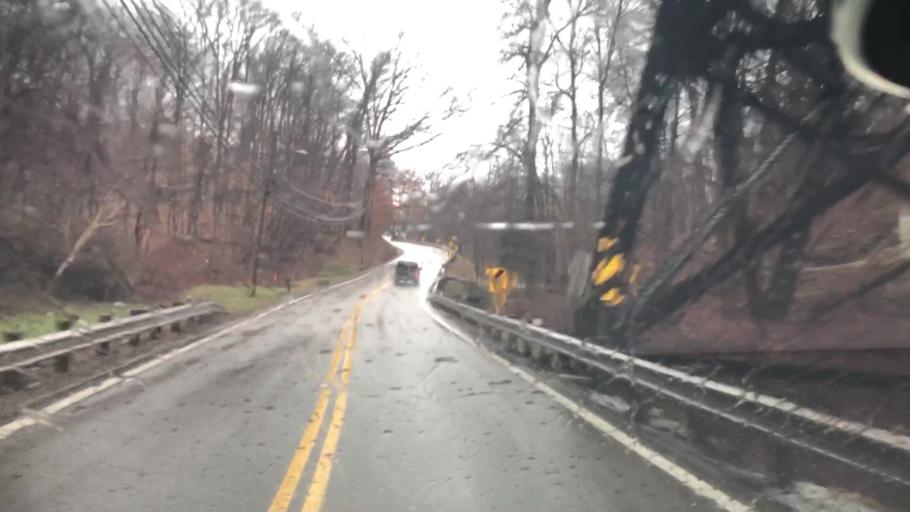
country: US
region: Ohio
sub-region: Belmont County
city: Saint Clairsville
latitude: 40.0884
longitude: -80.9095
